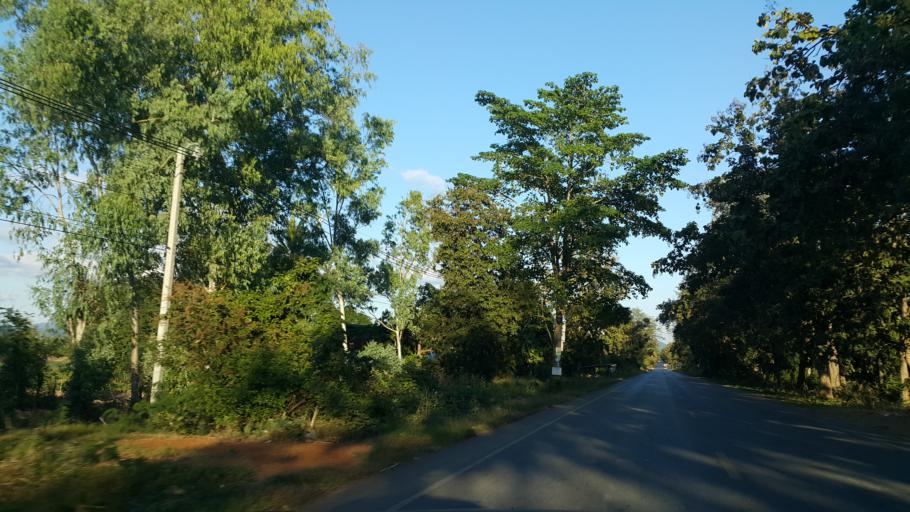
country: TH
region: Sukhothai
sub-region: Amphoe Si Satchanalai
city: Si Satchanalai
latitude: 17.5410
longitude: 99.8188
